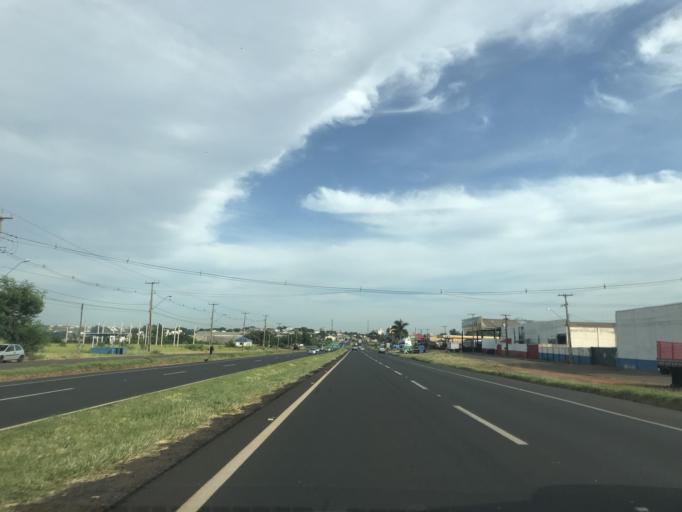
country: BR
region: Parana
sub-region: Mandaguacu
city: Mandaguacu
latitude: -23.3613
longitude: -52.0863
